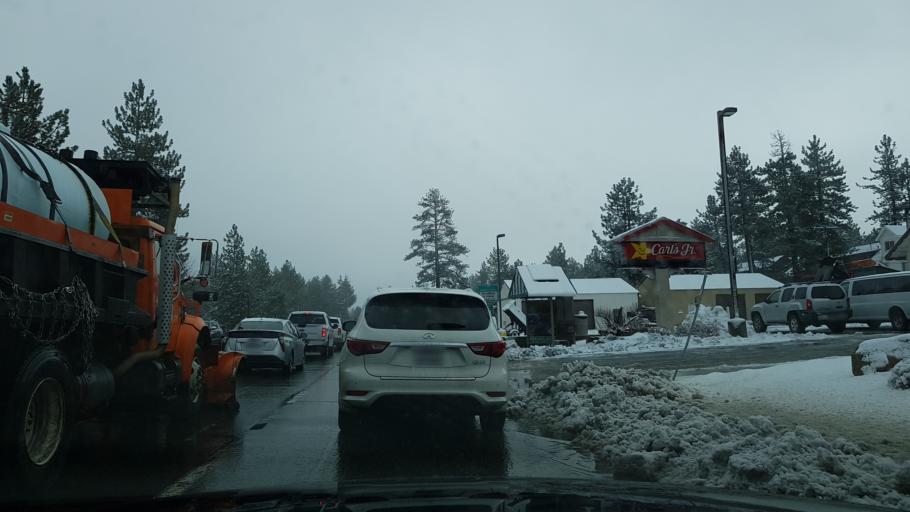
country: US
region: California
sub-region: San Bernardino County
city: Big Bear Lake
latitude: 34.2434
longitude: -116.8920
